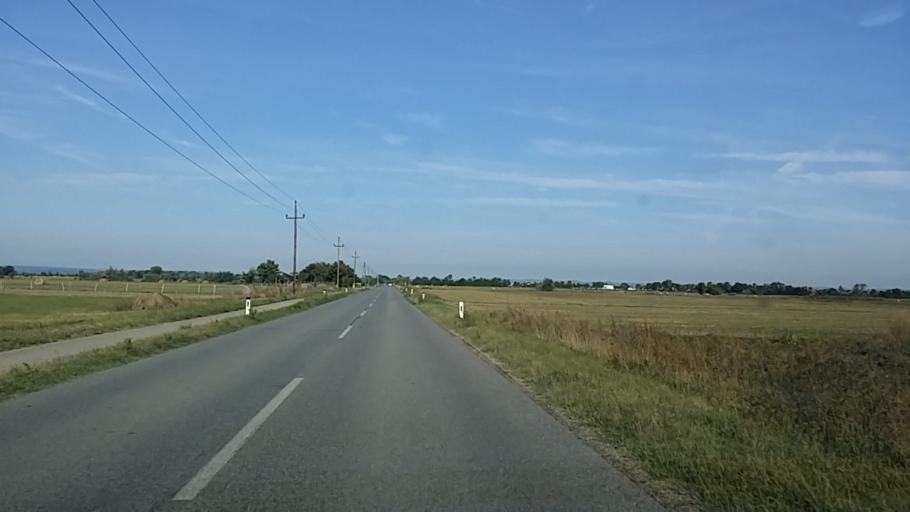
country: AT
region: Burgenland
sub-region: Politischer Bezirk Neusiedl am See
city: Apetlon
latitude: 47.7302
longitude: 16.8482
